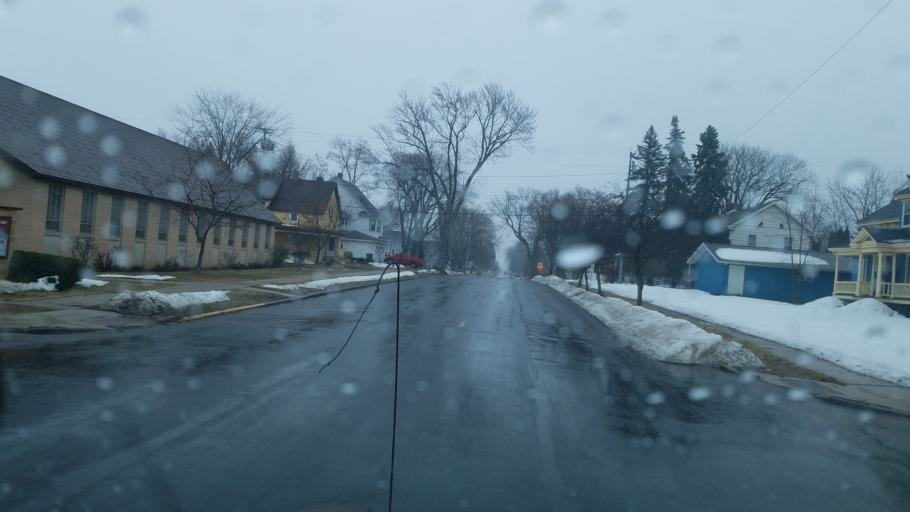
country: US
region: Wisconsin
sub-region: Wood County
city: Marshfield
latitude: 44.6635
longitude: -90.1709
